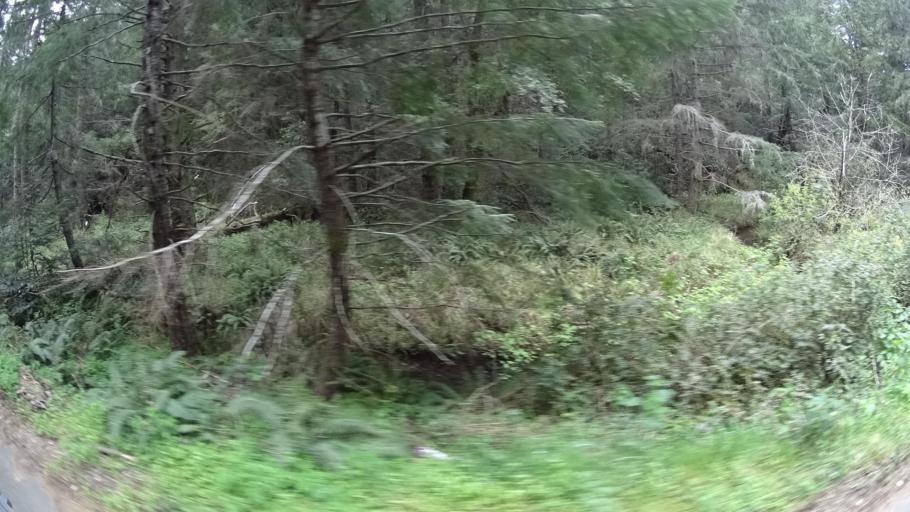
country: US
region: California
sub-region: Humboldt County
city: Redway
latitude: 40.0231
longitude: -124.0081
